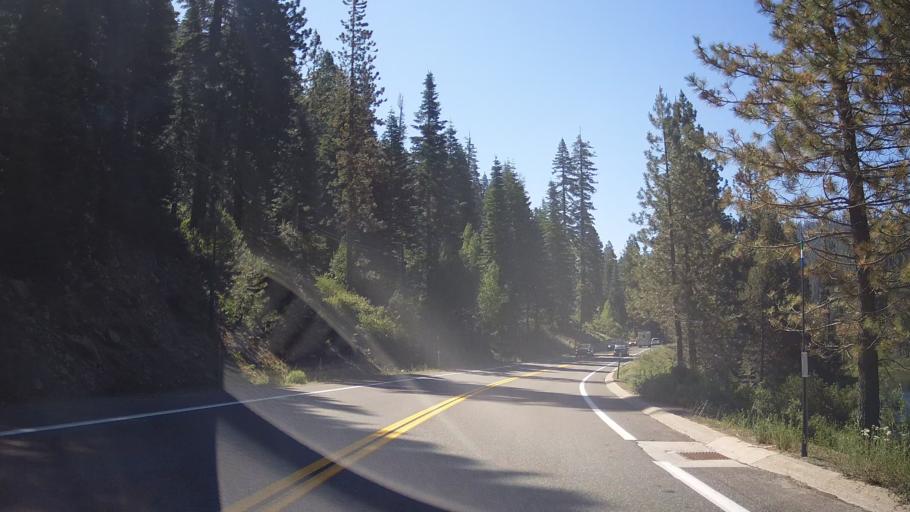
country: US
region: California
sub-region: Placer County
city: Sunnyside-Tahoe City
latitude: 39.1779
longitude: -120.1910
